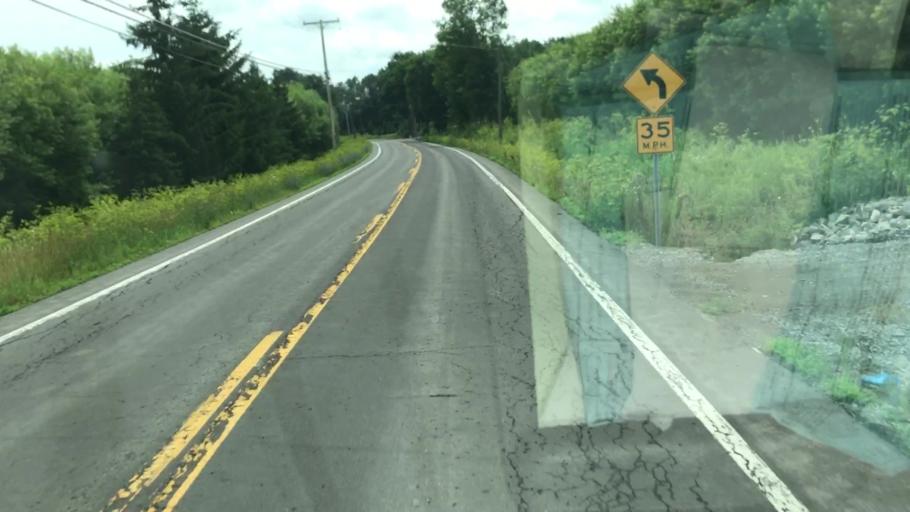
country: US
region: New York
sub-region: Onondaga County
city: Manlius
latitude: 42.9563
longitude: -75.9865
